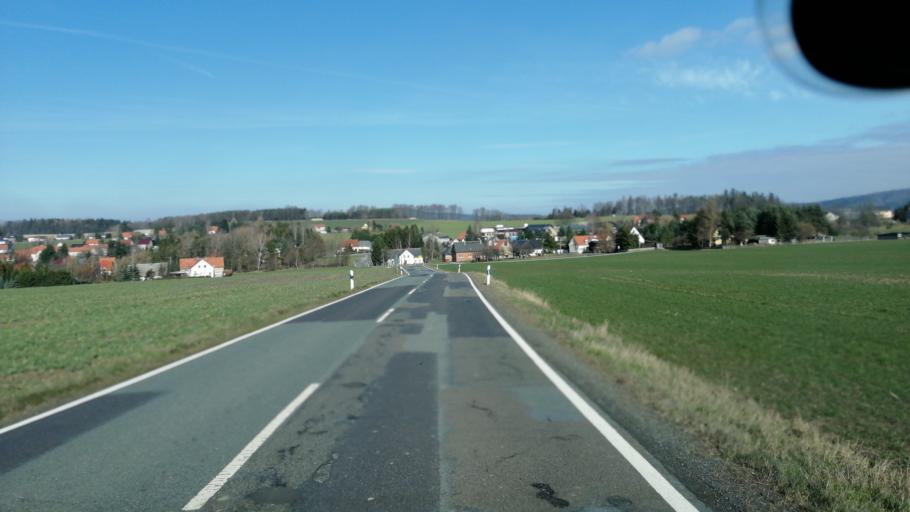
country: DE
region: Saxony
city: Beiersdorf
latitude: 51.0734
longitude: 14.5490
